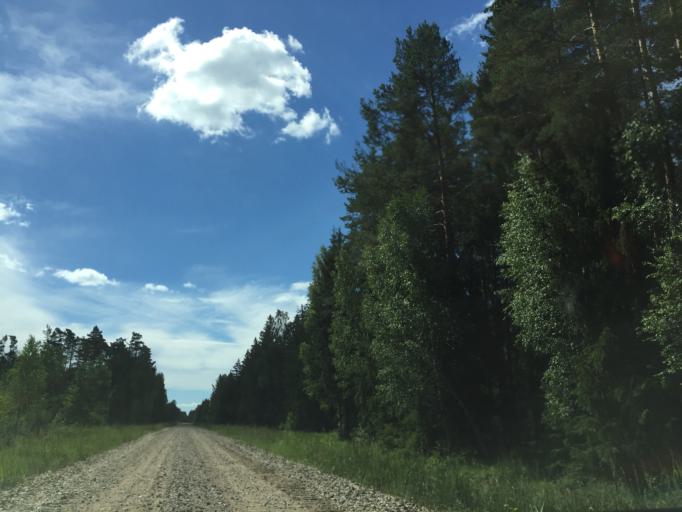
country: LV
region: Ventspils Rajons
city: Piltene
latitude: 57.2626
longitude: 21.8367
